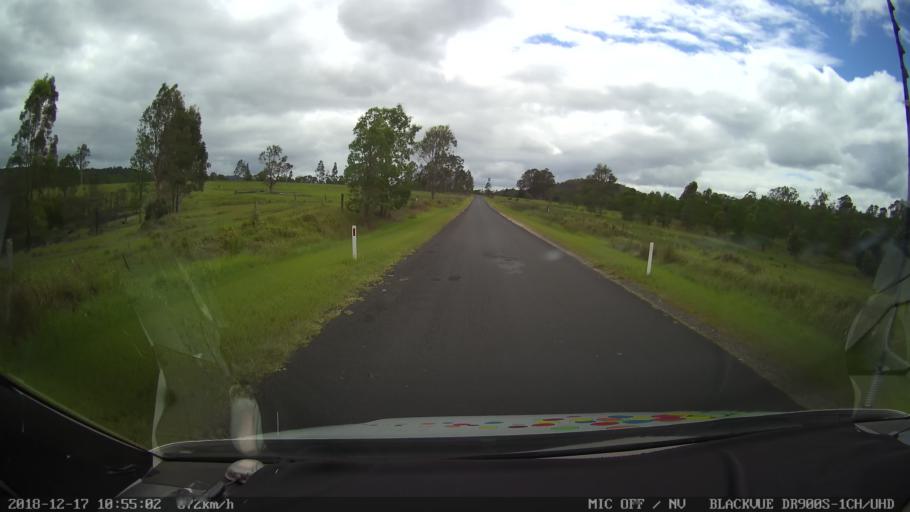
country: AU
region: New South Wales
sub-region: Tenterfield Municipality
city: Carrolls Creek
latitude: -28.8279
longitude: 152.5742
